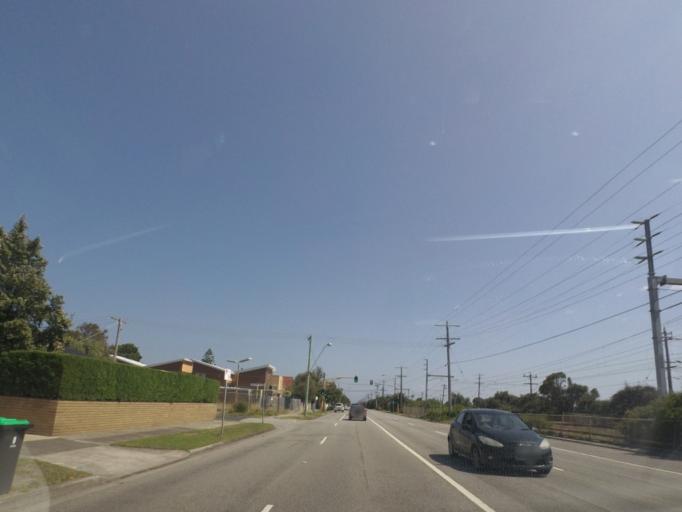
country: AU
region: Victoria
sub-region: Kingston
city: Chelsea
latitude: -38.0448
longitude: 145.1121
